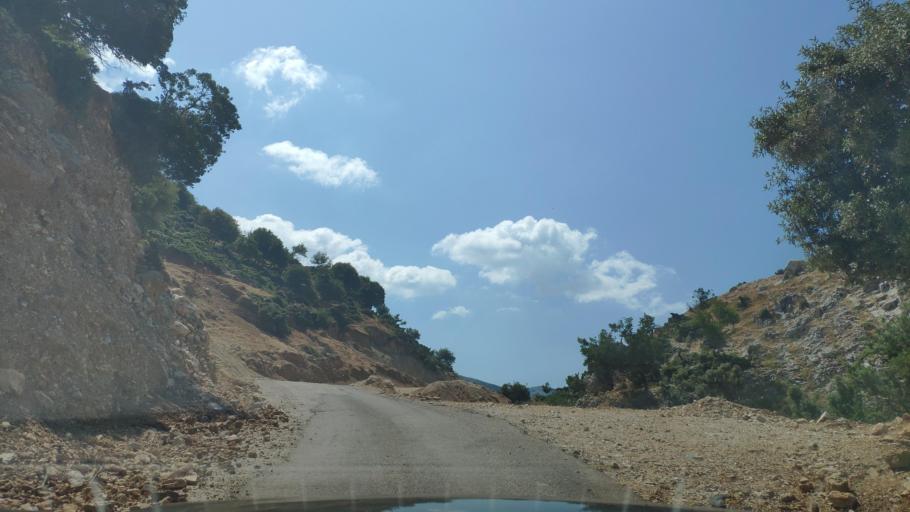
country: GR
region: West Greece
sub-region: Nomos Aitolias kai Akarnanias
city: Monastirakion
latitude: 38.8110
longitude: 20.9402
